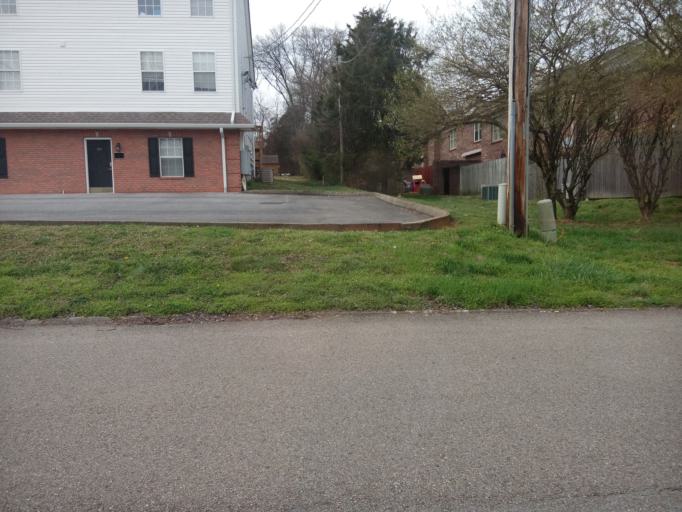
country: US
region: Tennessee
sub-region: Knox County
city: Farragut
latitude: 35.8984
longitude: -84.1245
